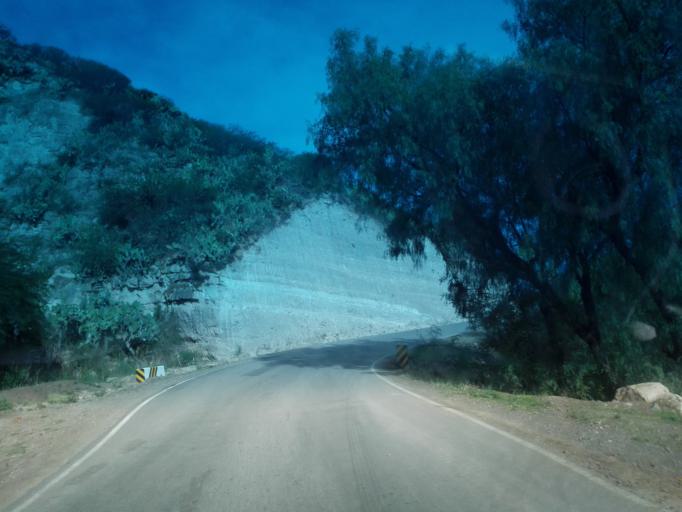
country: PE
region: Ayacucho
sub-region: Provincia de Huamanga
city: Pacaycasa
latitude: -13.0754
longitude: -74.2418
